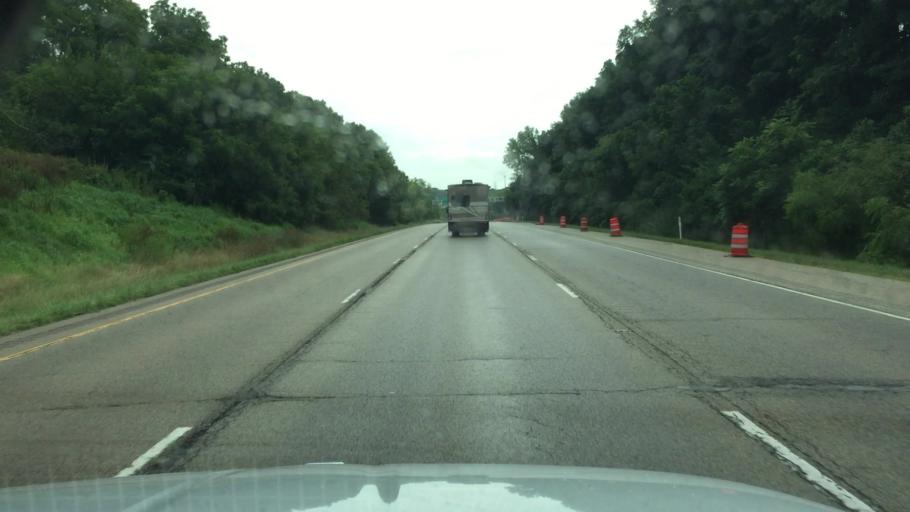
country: US
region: Illinois
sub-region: Peoria County
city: Bellevue
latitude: 40.7453
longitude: -89.6810
